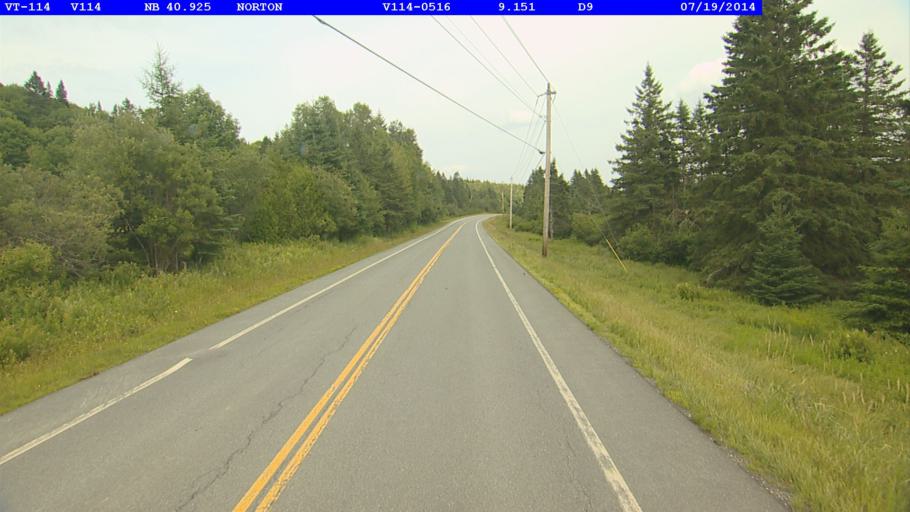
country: CA
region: Quebec
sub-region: Estrie
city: Coaticook
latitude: 44.9960
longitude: -71.7227
